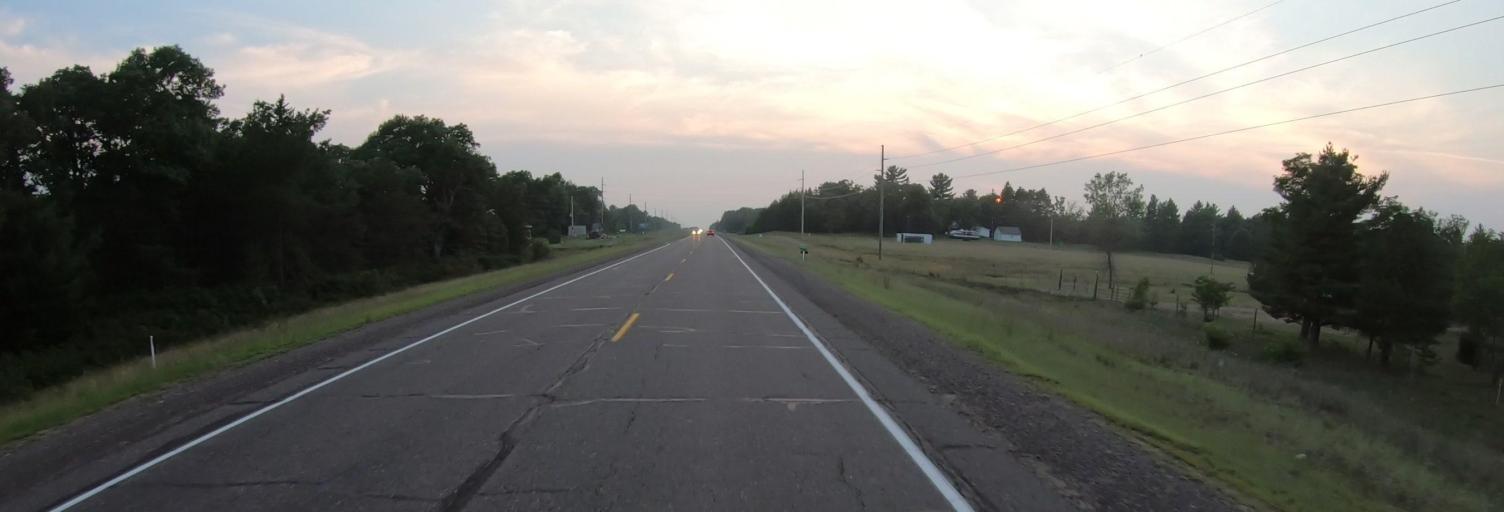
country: US
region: Wisconsin
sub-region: Burnett County
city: Grantsburg
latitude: 45.7732
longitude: -92.7332
